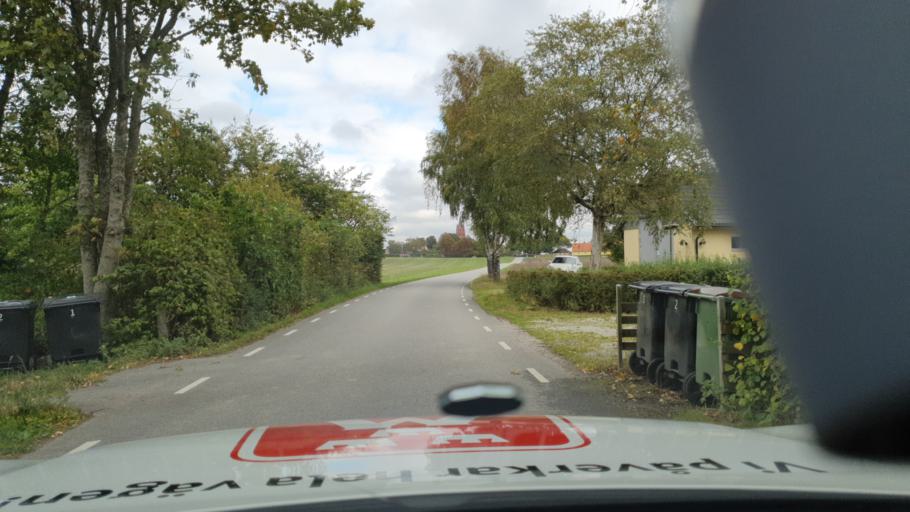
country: SE
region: Skane
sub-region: Vellinge Kommun
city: Vellinge
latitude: 55.4465
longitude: 13.0744
